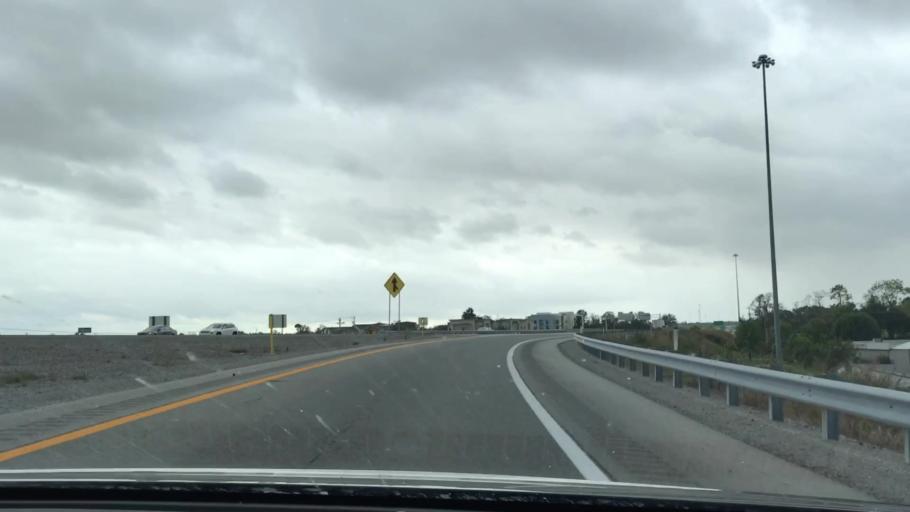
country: US
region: Kentucky
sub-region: Christian County
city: Hopkinsville
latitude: 36.8296
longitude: -87.4754
